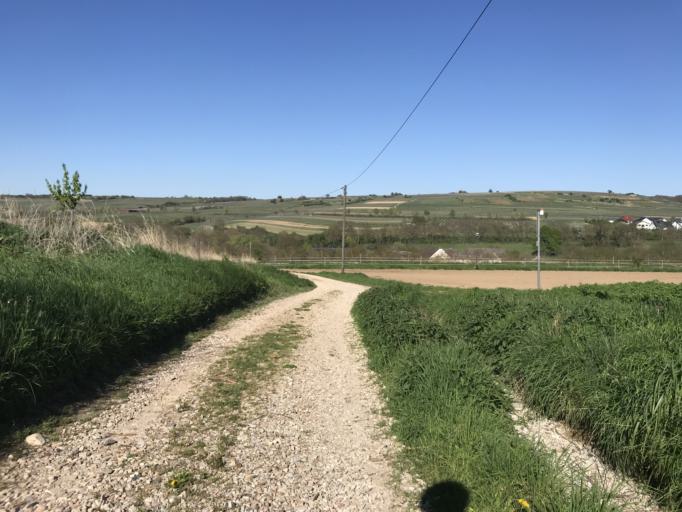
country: DE
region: Rheinland-Pfalz
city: Bubenheim
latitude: 49.9445
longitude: 8.0652
